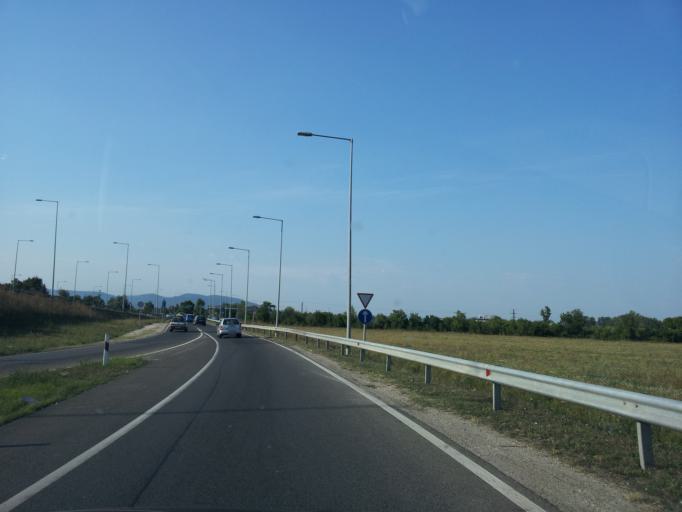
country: HU
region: Pest
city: Budakalasz
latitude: 47.6131
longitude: 19.0655
